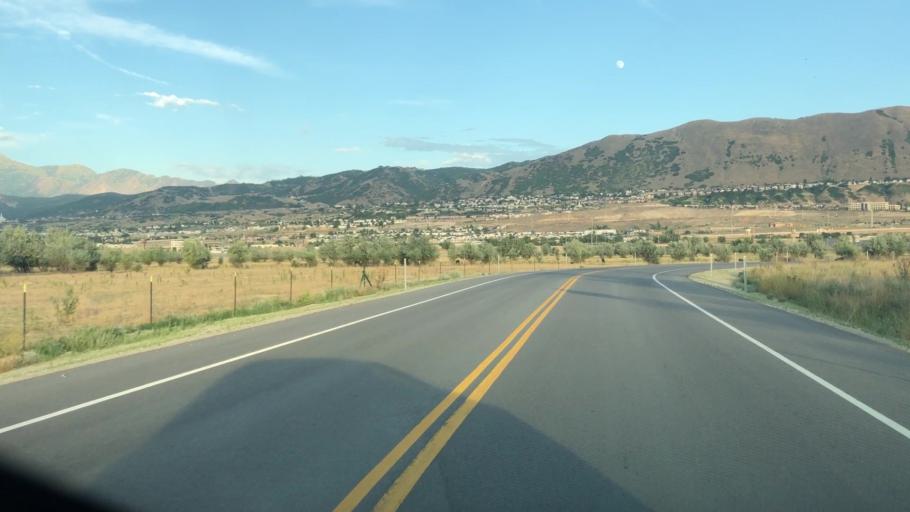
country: US
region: Utah
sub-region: Salt Lake County
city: Bluffdale
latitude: 40.4985
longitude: -111.9042
